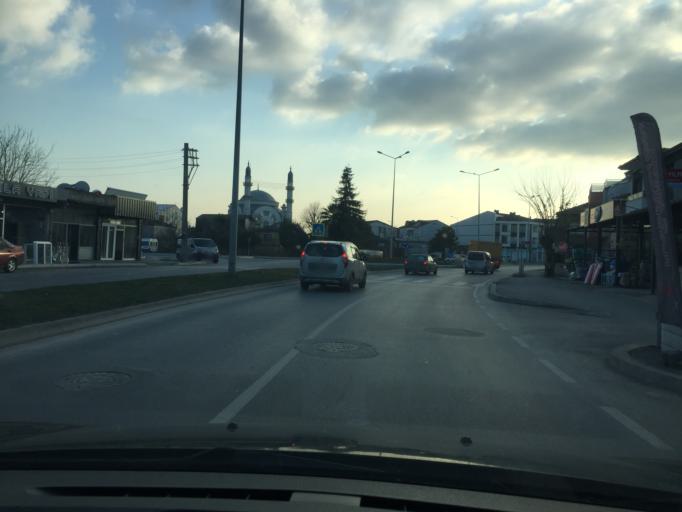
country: TR
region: Sakarya
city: Adapazari
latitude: 40.7905
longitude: 30.4073
